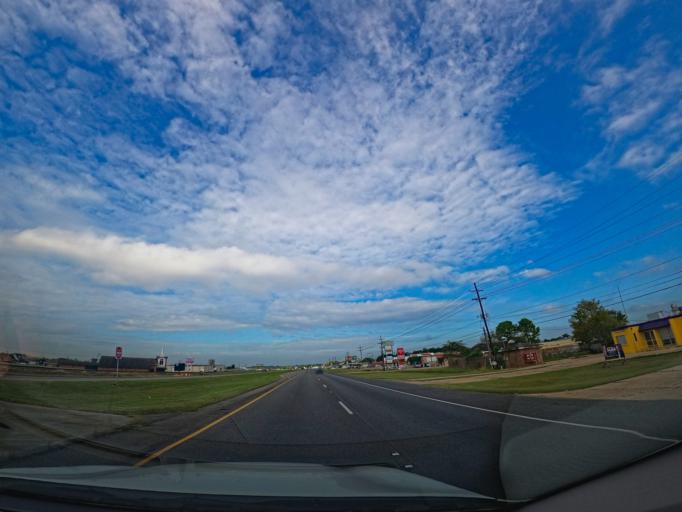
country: US
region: Louisiana
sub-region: Saint Mary Parish
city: Patterson
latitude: 29.6835
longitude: -91.3007
